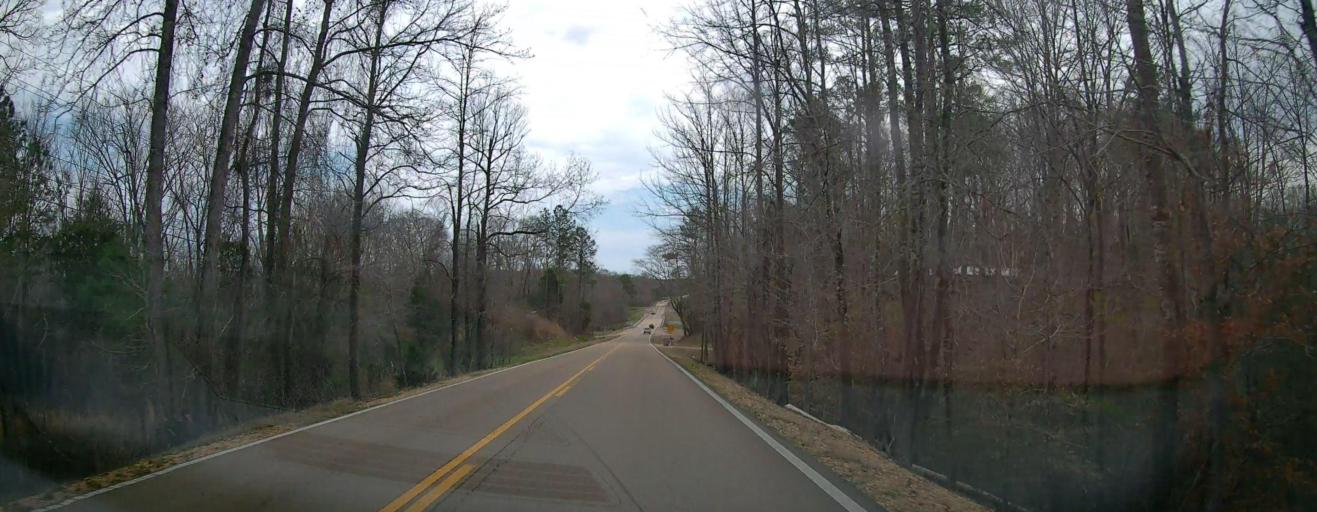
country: US
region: Mississippi
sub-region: Itawamba County
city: Fulton
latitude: 34.2462
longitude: -88.2900
